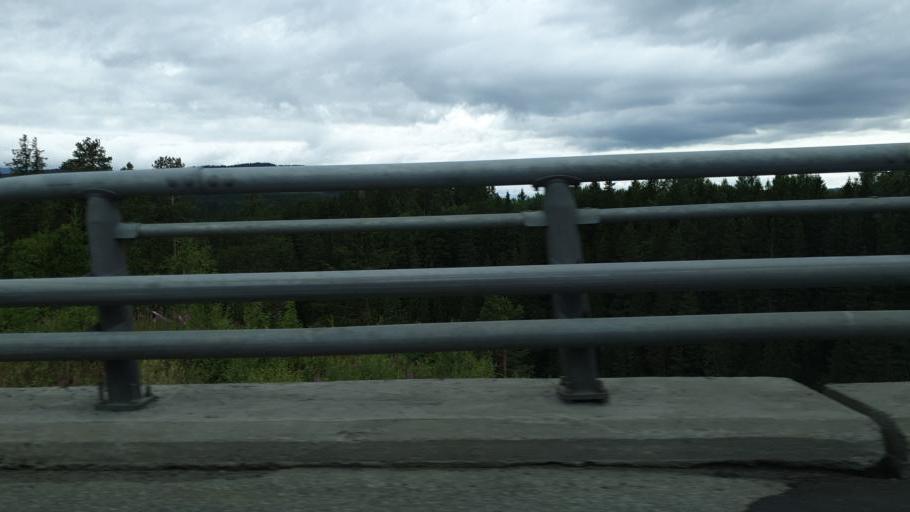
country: NO
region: Sor-Trondelag
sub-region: Rennebu
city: Berkak
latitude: 62.8043
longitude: 10.0334
